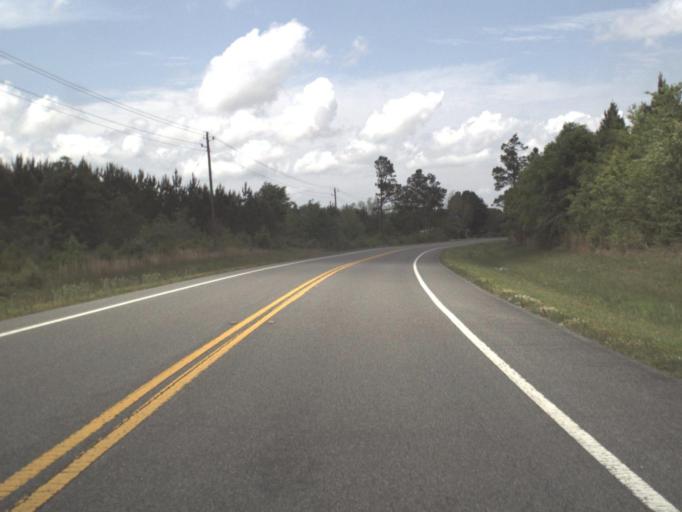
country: US
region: Florida
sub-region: Santa Rosa County
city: Point Baker
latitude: 30.8089
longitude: -87.1278
